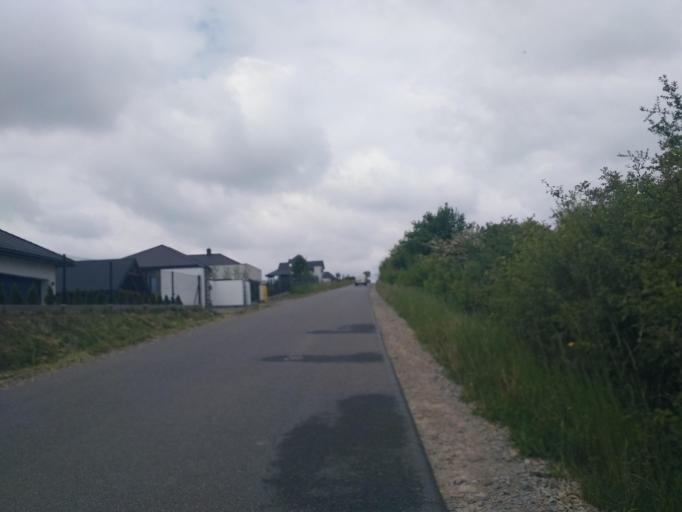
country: PL
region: Subcarpathian Voivodeship
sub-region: Powiat krosnienski
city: Chorkowka
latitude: 49.6693
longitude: 21.6787
